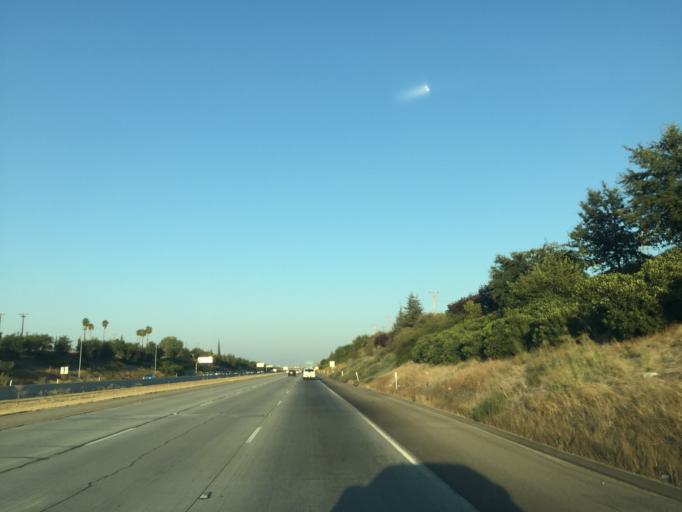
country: US
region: California
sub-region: Fresno County
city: Sunnyside
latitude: 36.7531
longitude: -119.7160
